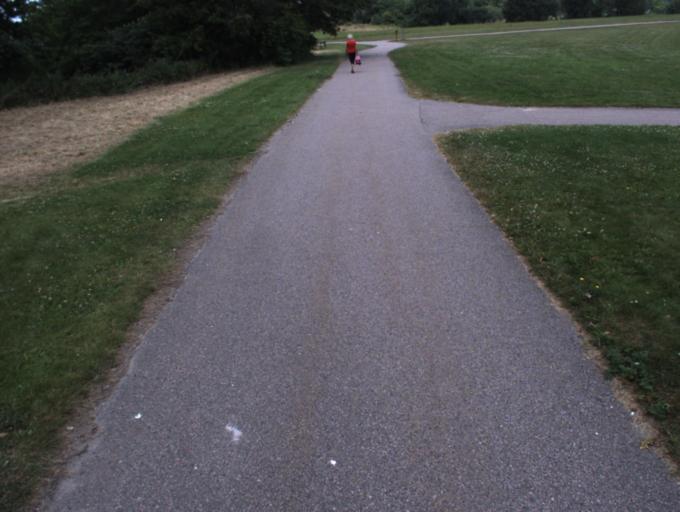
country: SE
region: Skane
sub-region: Helsingborg
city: Rydeback
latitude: 55.9625
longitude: 12.7598
